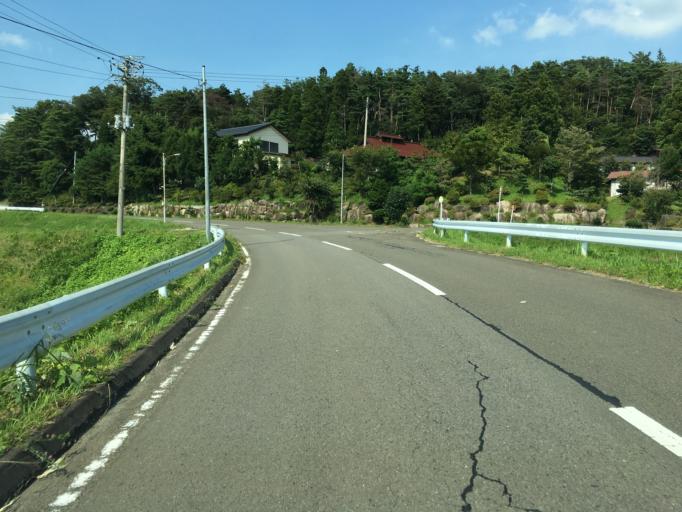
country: JP
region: Fukushima
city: Nihommatsu
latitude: 37.5767
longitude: 140.3847
